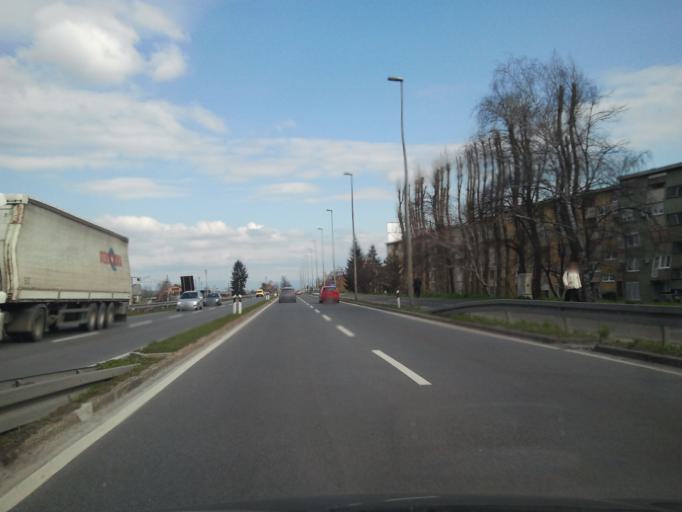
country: HR
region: Karlovacka
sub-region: Grad Karlovac
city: Karlovac
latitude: 45.4917
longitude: 15.5475
